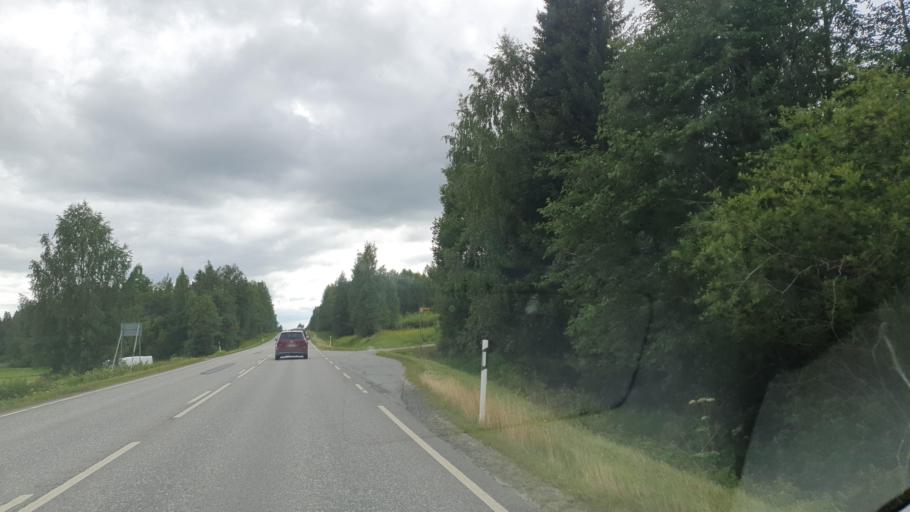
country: FI
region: Northern Savo
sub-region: Ylae-Savo
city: Sonkajaervi
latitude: 63.7203
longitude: 27.3677
